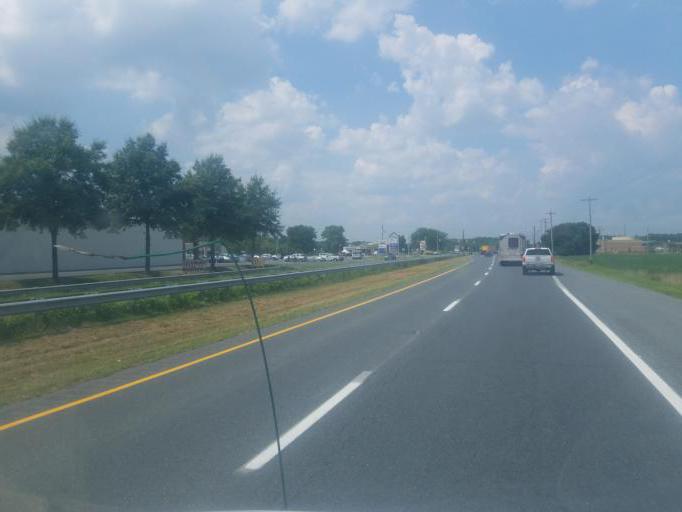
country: US
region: Maryland
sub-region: Worcester County
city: Berlin
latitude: 38.3334
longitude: -75.2101
